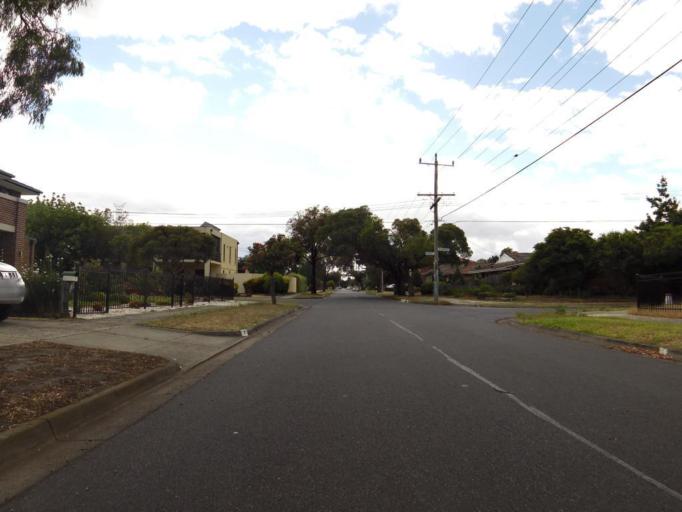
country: AU
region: Victoria
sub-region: Monash
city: Notting Hill
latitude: -37.8961
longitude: 145.1591
